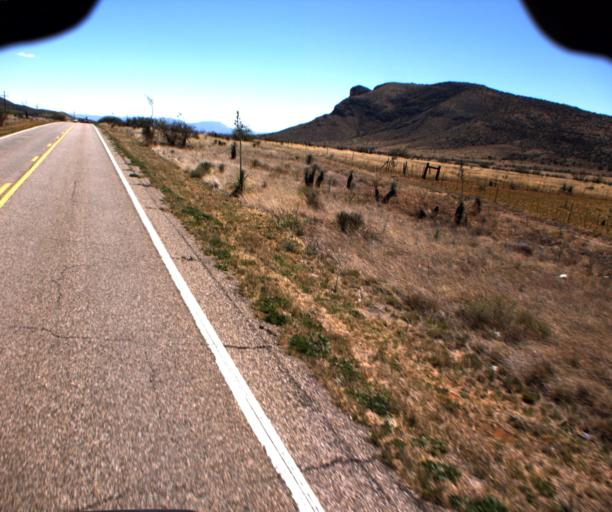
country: US
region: Arizona
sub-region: Cochise County
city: Huachuca City
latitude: 31.7105
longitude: -110.4506
